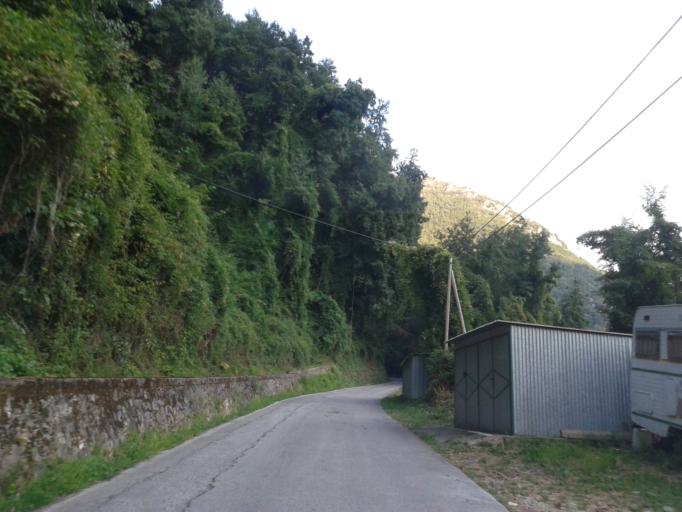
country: IT
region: Tuscany
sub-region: Provincia di Lucca
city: Pontestazzemese
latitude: 43.9660
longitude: 10.3314
